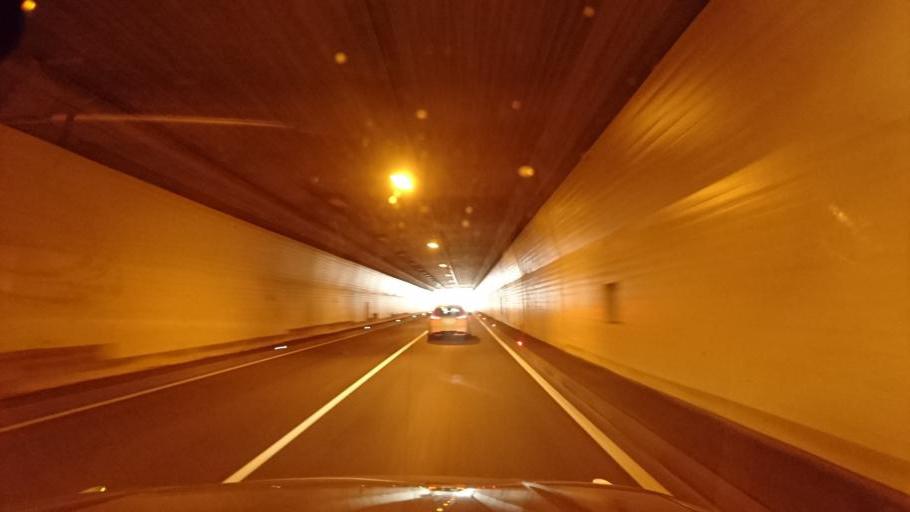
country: AT
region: Tyrol
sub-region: Politischer Bezirk Landeck
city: Ischgl
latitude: 47.0180
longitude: 10.3005
